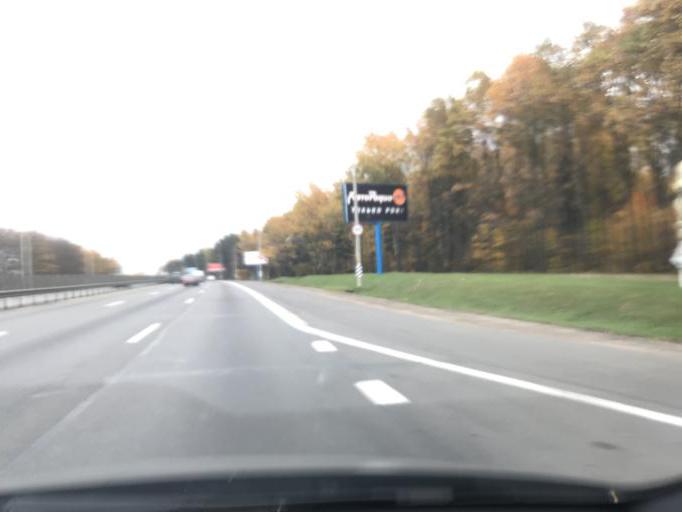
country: BY
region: Minsk
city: Hatava
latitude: 53.8335
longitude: 27.6400
